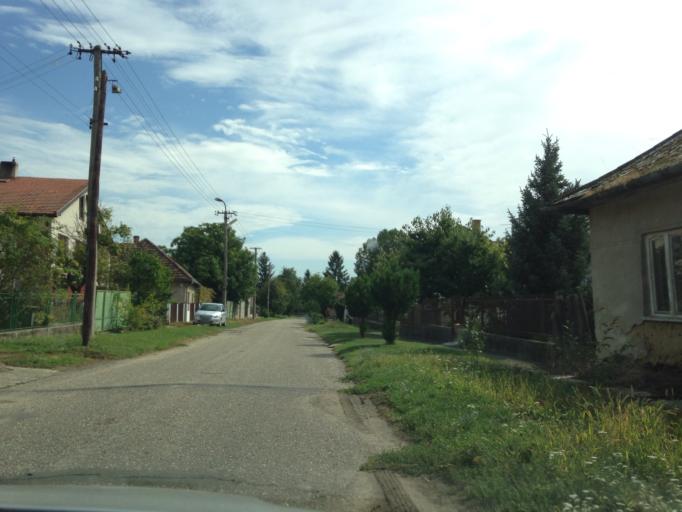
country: SK
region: Nitriansky
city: Svodin
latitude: 47.9034
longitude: 18.4215
